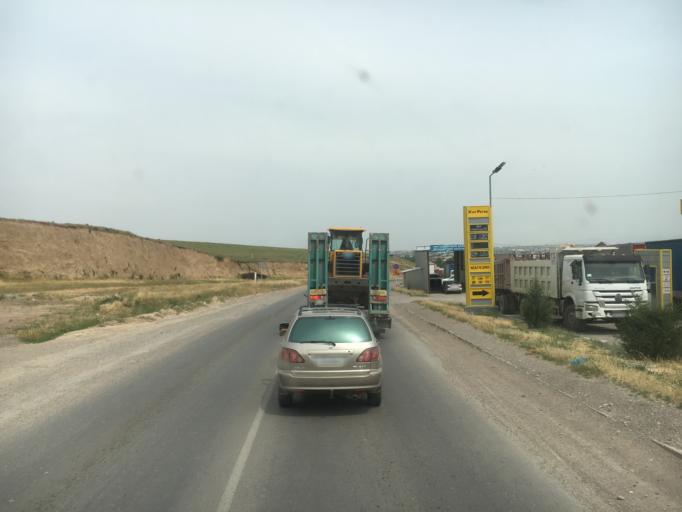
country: KZ
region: Ongtustik Qazaqstan
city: Shymkent
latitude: 42.3280
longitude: 69.5137
